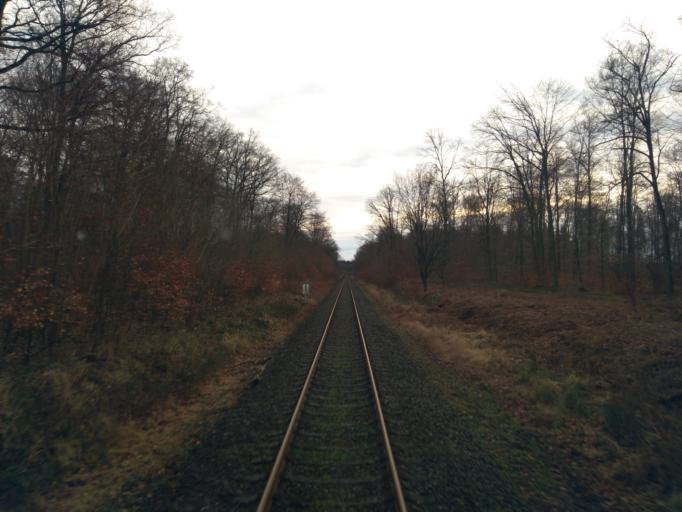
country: DE
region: Lower Saxony
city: Schwienau
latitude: 53.0117
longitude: 10.4641
